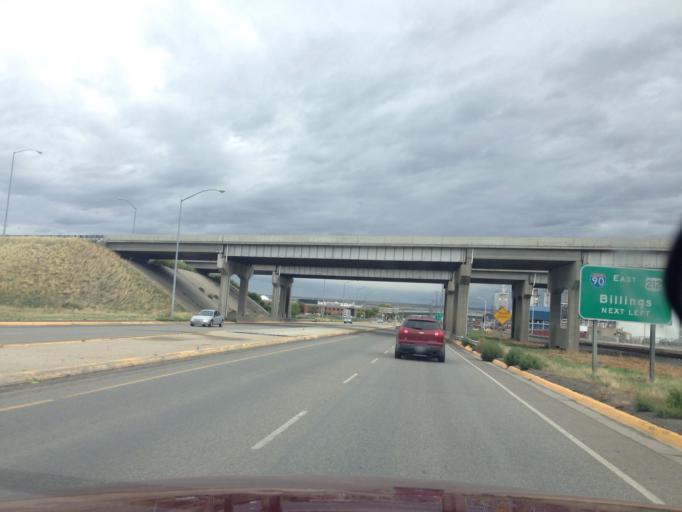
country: US
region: Montana
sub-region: Yellowstone County
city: Laurel
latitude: 45.6633
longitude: -108.7704
